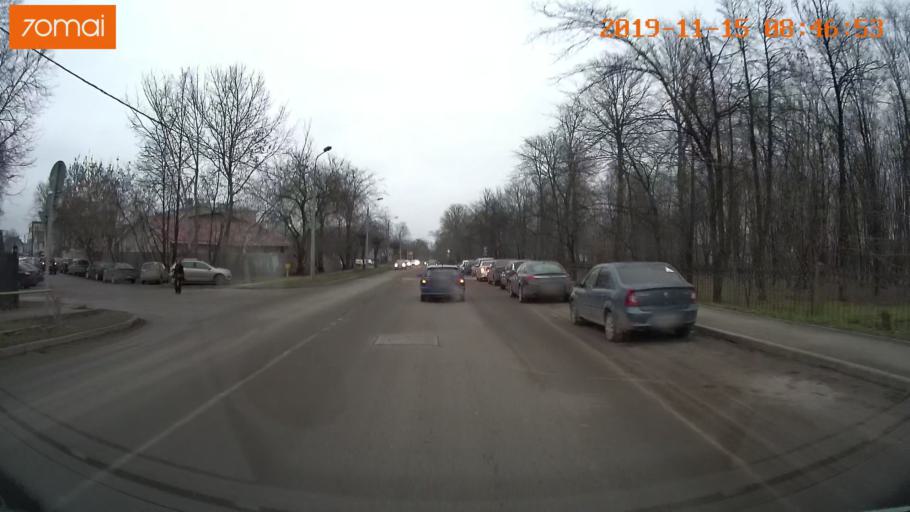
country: RU
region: Vologda
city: Cherepovets
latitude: 59.1192
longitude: 37.9094
